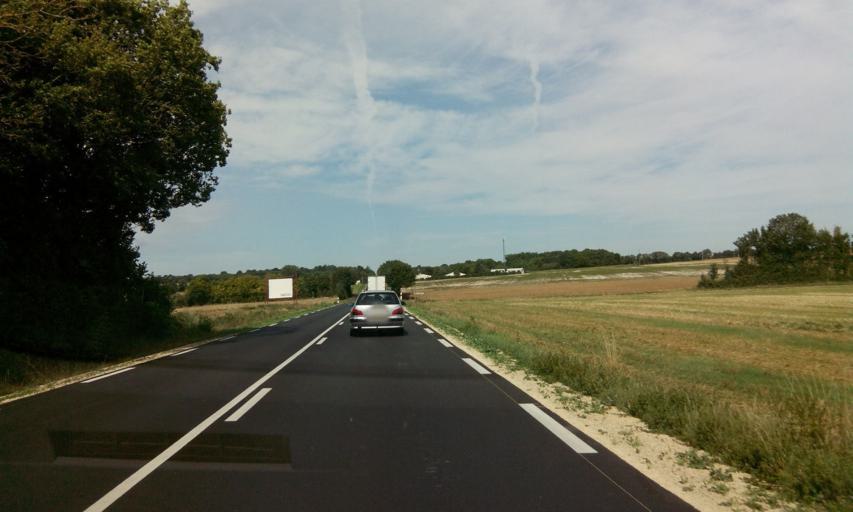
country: FR
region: Poitou-Charentes
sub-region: Departement des Deux-Sevres
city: Sauze-Vaussais
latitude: 46.1460
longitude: 0.0764
